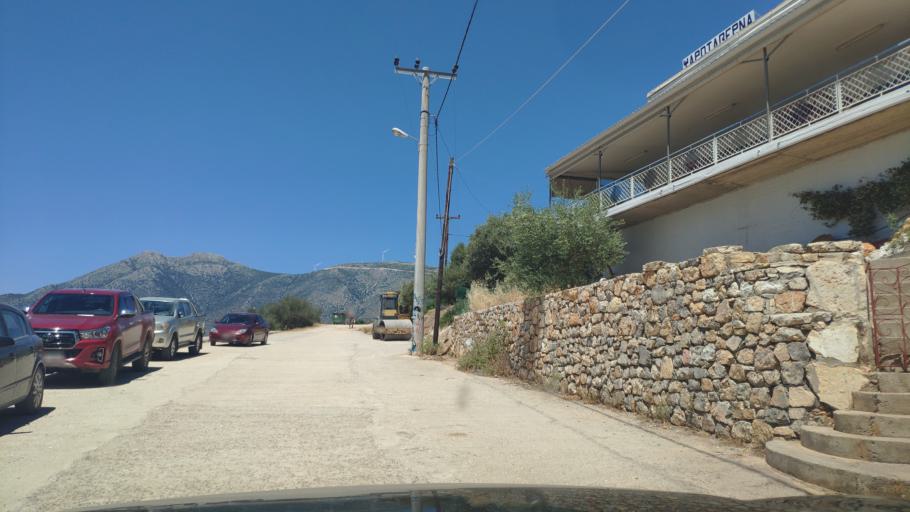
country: GR
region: Central Greece
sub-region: Nomos Voiotias
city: Kaparellion
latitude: 38.1837
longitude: 23.1426
